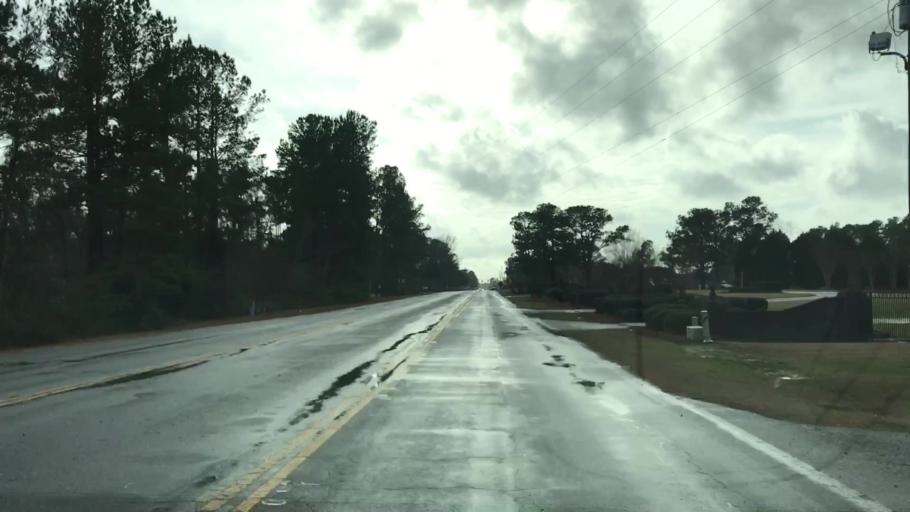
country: US
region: South Carolina
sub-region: Williamsburg County
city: Andrews
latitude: 33.4610
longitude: -79.5724
